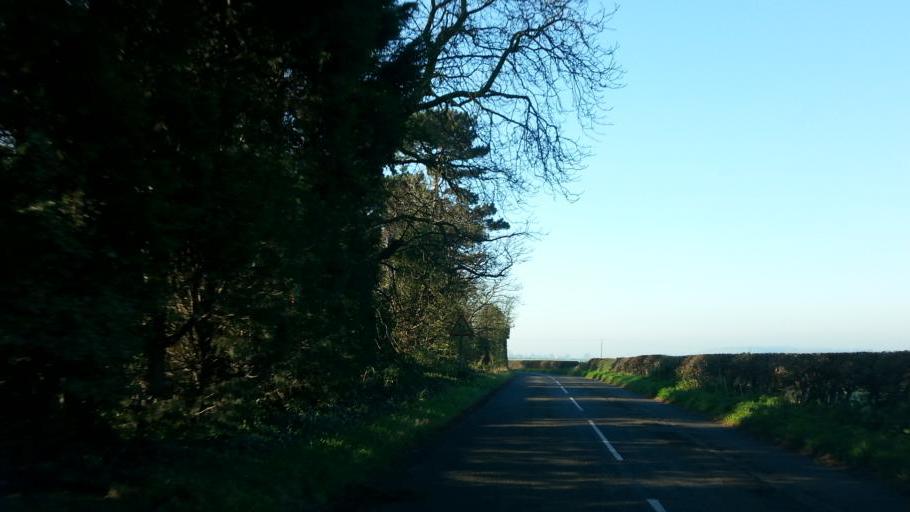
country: GB
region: England
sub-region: Nottinghamshire
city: Newark on Trent
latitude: 53.1040
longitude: -0.8251
